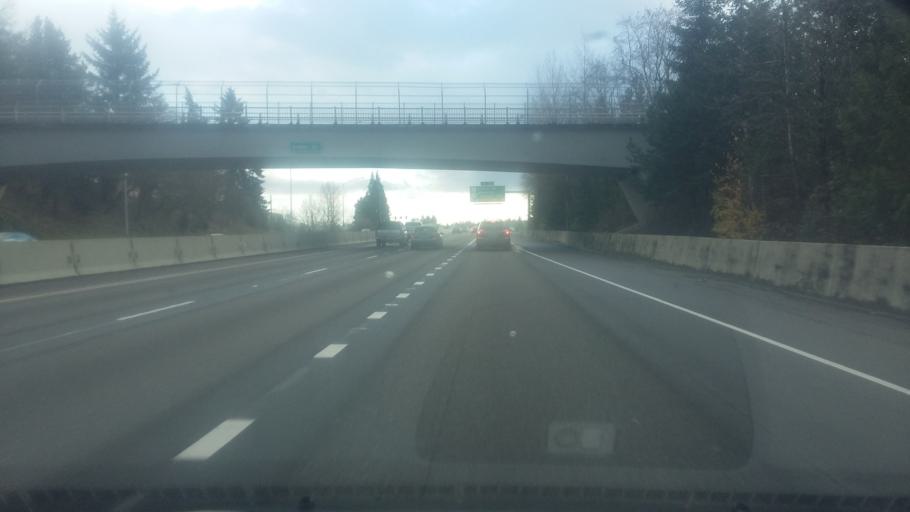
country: US
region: Oregon
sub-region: Washington County
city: Cedar Hills
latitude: 45.4953
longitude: -122.7916
